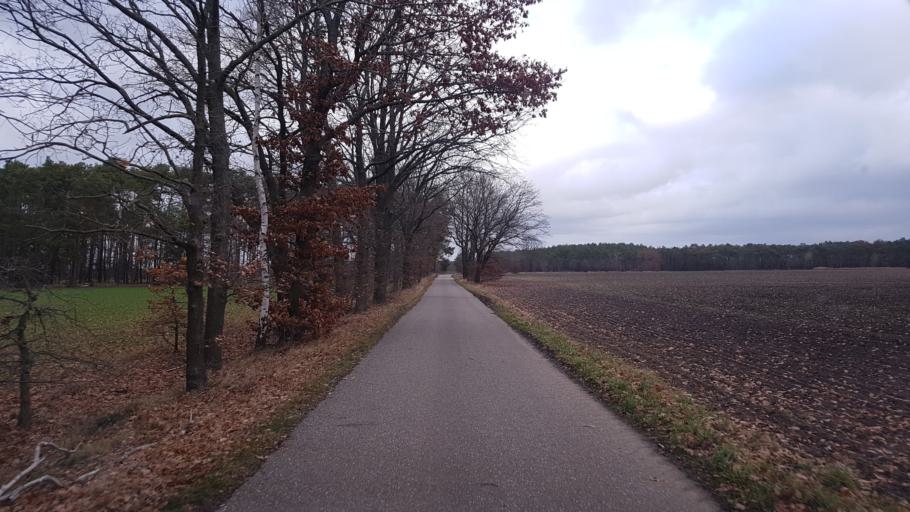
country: DE
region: Brandenburg
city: Ruckersdorf
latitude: 51.5958
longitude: 13.6288
